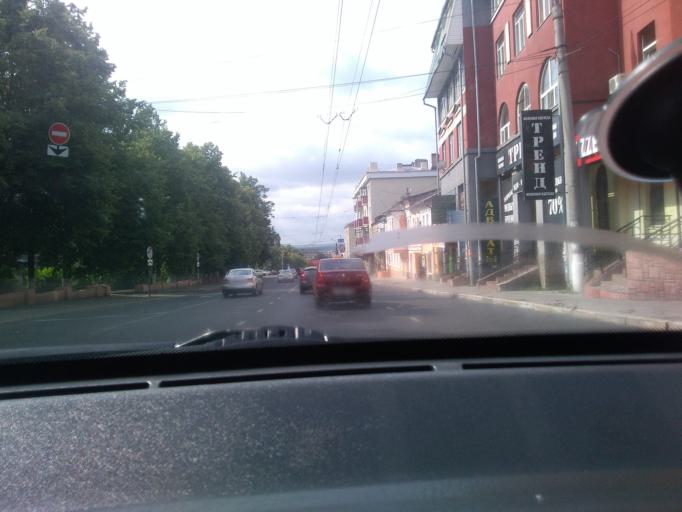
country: RU
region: Kursk
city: Kursk
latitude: 51.7315
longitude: 36.1903
